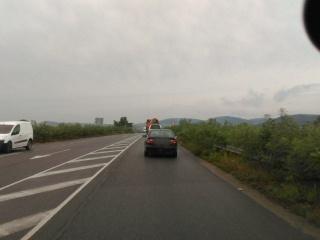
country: BG
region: Plovdiv
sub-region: Obshtina Karlovo
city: Karlovo
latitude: 42.5549
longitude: 24.8304
